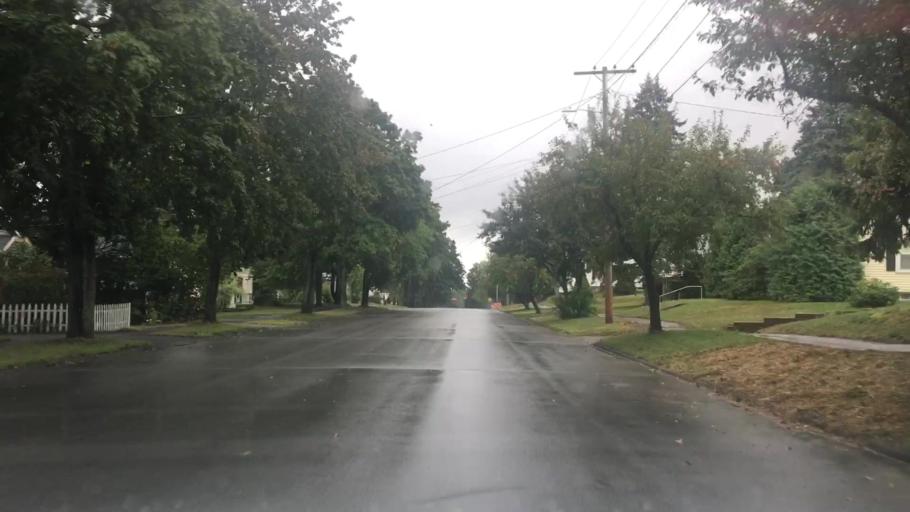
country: US
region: Maine
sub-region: Penobscot County
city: Brewer
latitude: 44.8163
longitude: -68.7602
